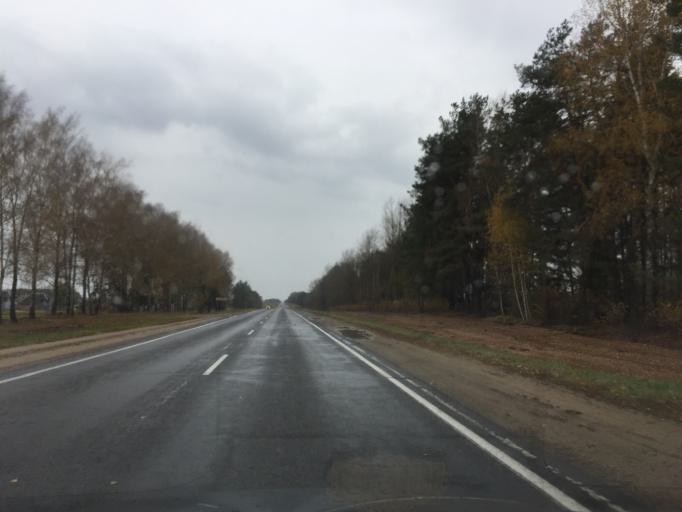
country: BY
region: Mogilev
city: Slawharad
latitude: 53.3985
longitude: 30.9176
